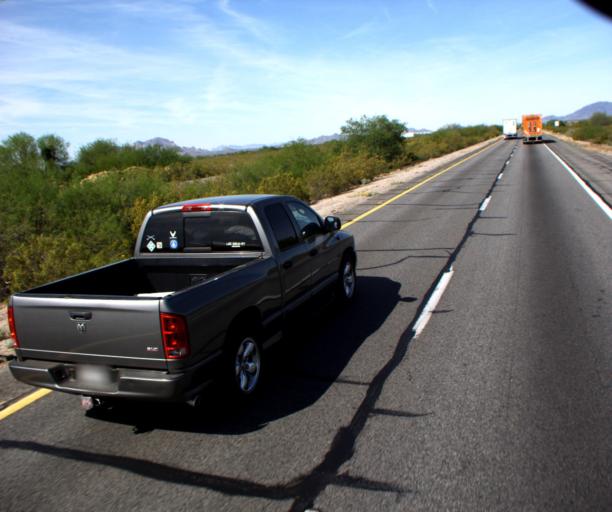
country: US
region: Arizona
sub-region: Maricopa County
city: Buckeye
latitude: 33.4847
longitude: -112.8792
